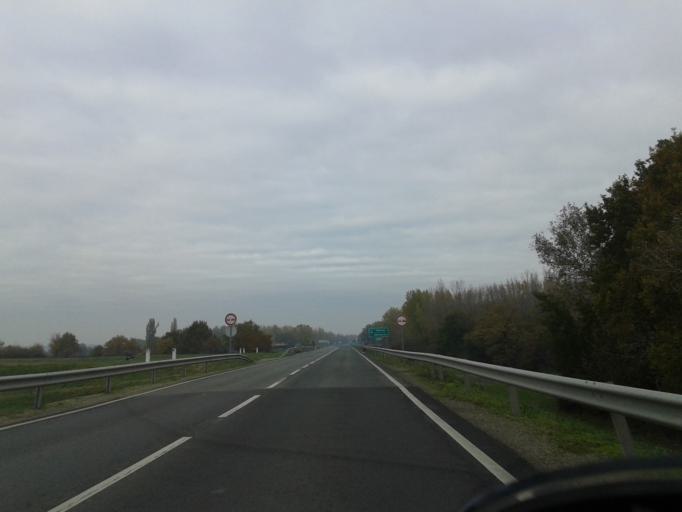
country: HU
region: Fejer
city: Adony
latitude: 47.1366
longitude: 18.8631
